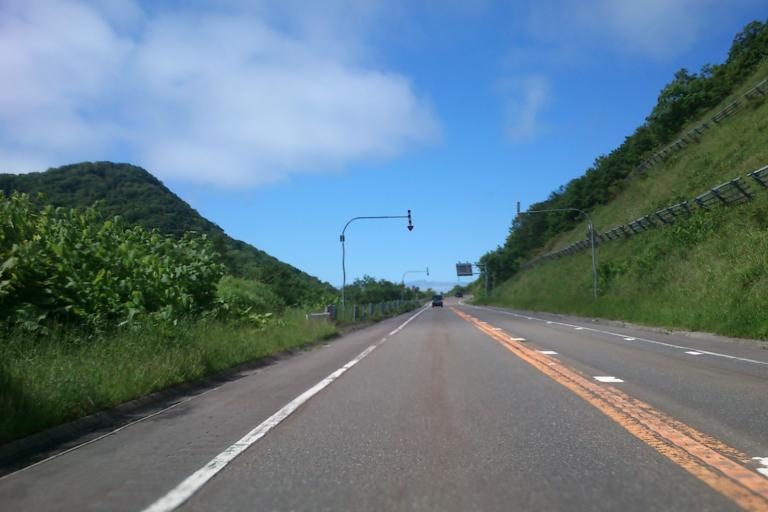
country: JP
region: Hokkaido
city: Ishikari
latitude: 43.4835
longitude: 141.3992
